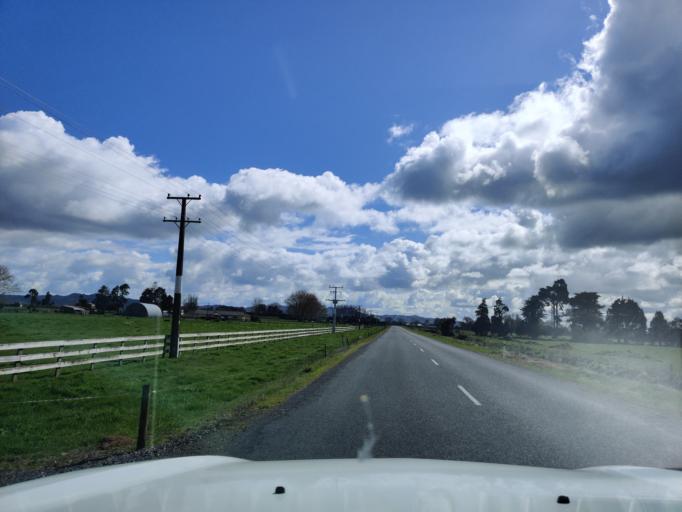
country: NZ
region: Waikato
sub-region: Waikato District
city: Ngaruawahia
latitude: -37.5926
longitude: 175.2924
